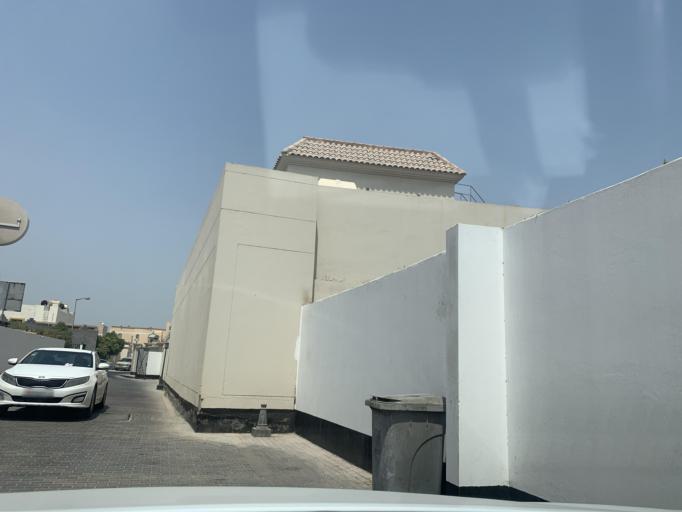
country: BH
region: Manama
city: Jidd Hafs
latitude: 26.2195
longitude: 50.5011
